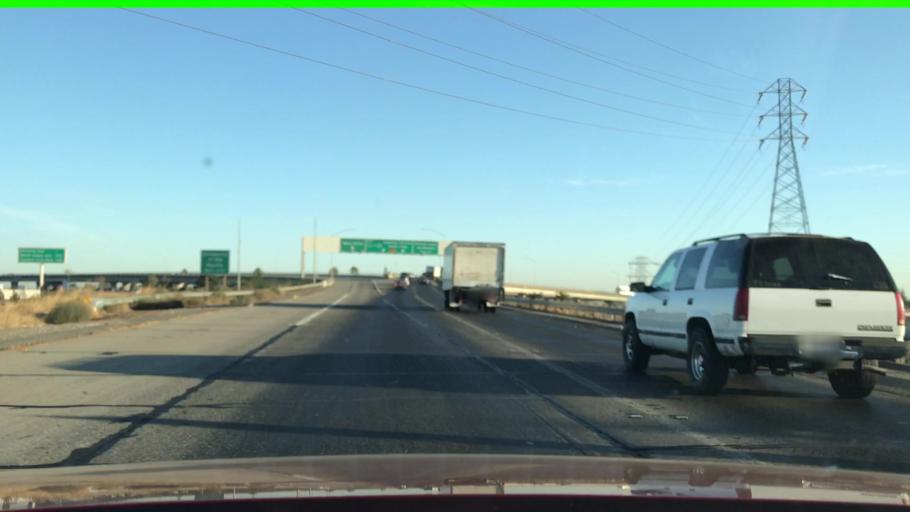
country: US
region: California
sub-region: San Joaquin County
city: Stockton
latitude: 37.9440
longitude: -121.2984
